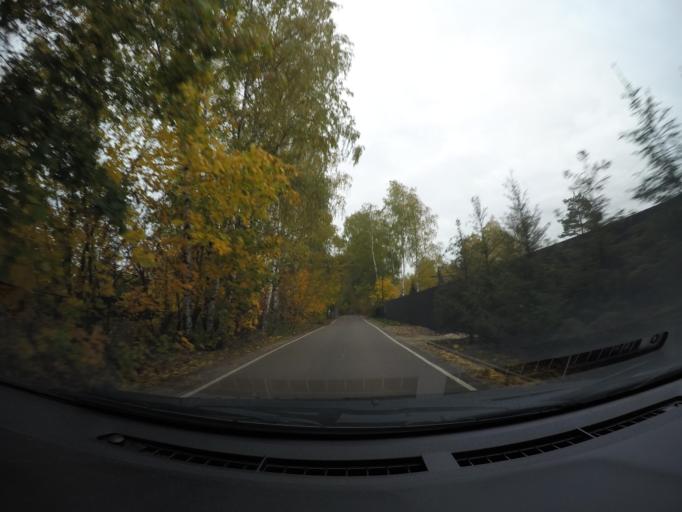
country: RU
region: Moskovskaya
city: Imeni Vorovskogo
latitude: 55.7315
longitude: 38.3110
